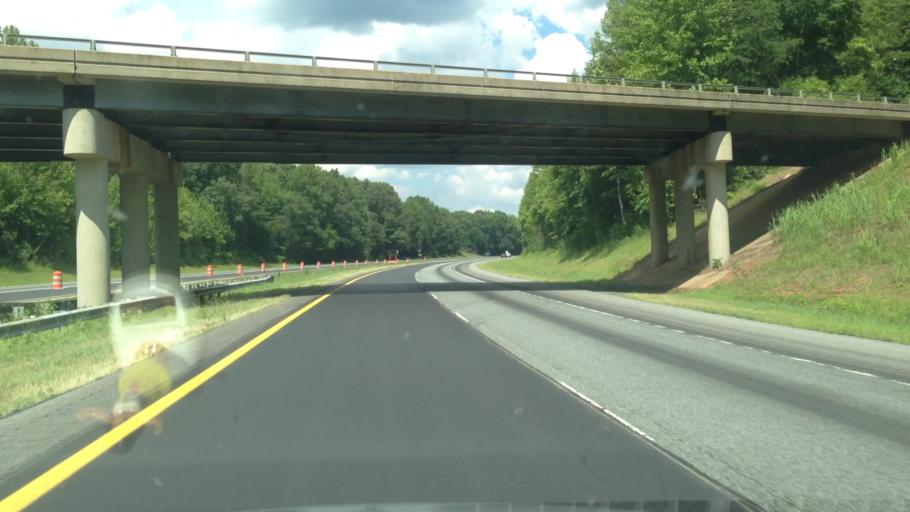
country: US
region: North Carolina
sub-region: Rockingham County
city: Reidsville
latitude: 36.4434
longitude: -79.5692
